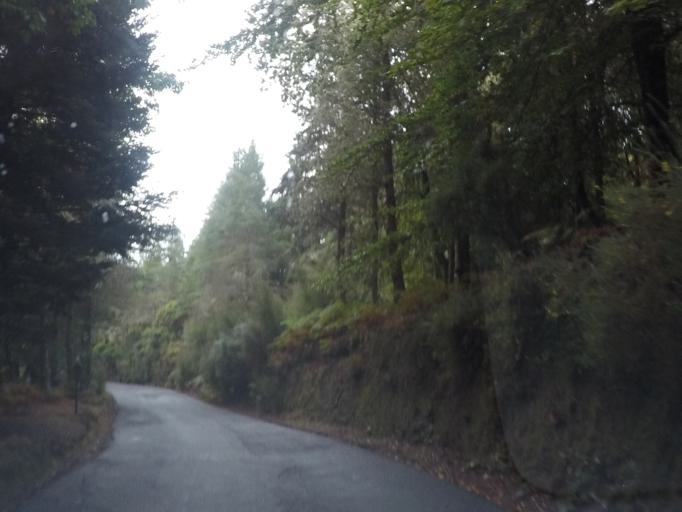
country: PT
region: Madeira
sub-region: Funchal
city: Nossa Senhora do Monte
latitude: 32.7042
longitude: -16.8820
